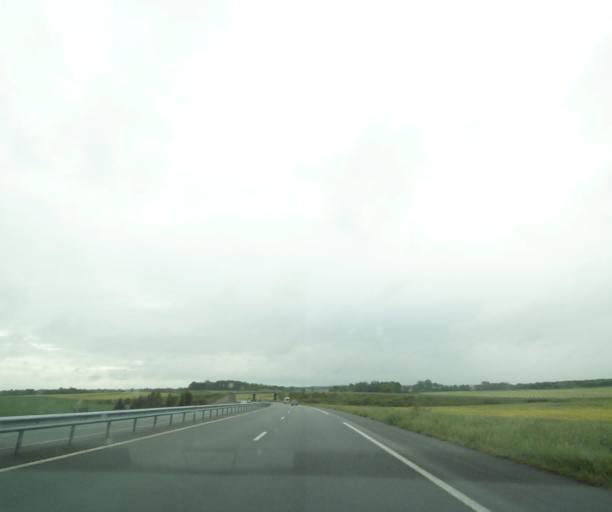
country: FR
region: Poitou-Charentes
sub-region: Departement de la Charente-Maritime
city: Nieul-les-Saintes
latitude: 45.6976
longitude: -0.7431
